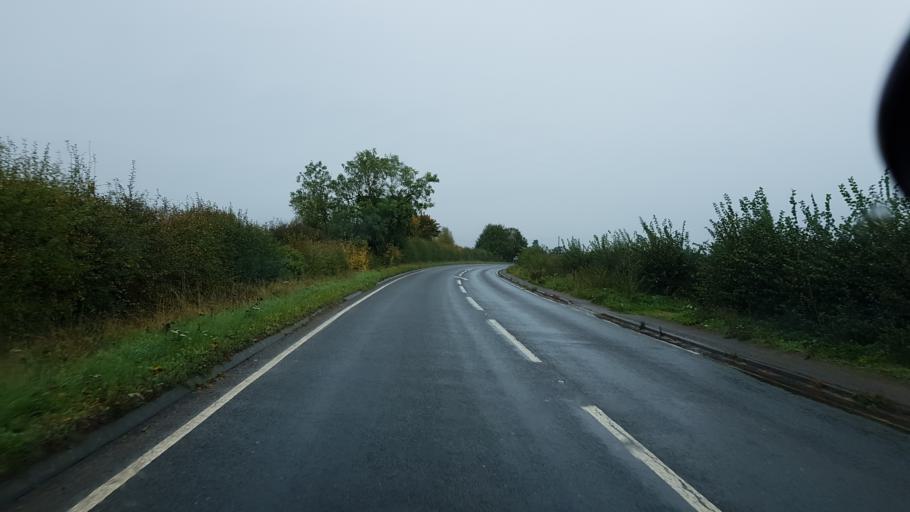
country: GB
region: England
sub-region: Worcestershire
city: Upton upon Severn
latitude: 52.0557
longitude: -2.1911
